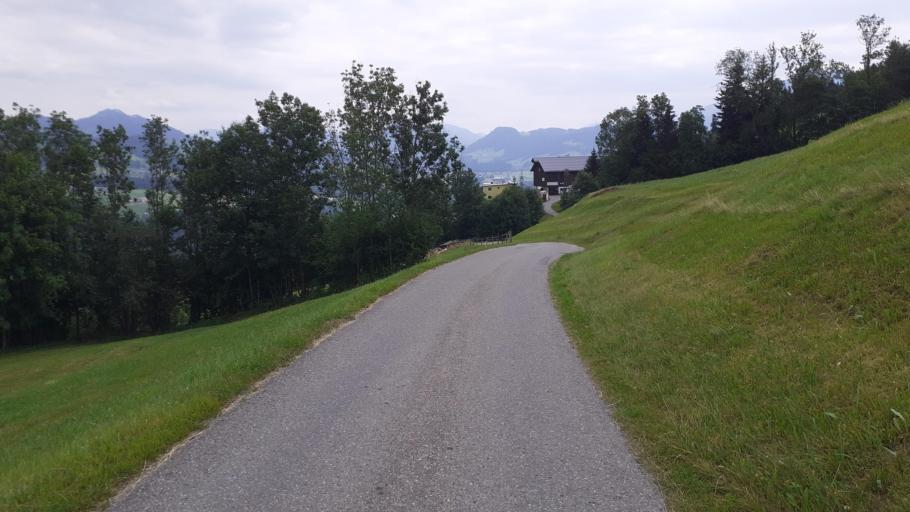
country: AT
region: Vorarlberg
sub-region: Politischer Bezirk Bregenz
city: Doren
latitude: 47.4569
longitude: 9.8593
